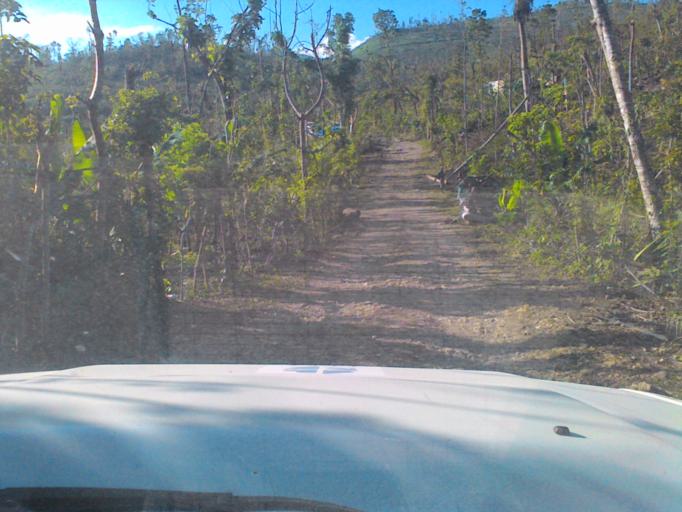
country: HT
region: Grandans
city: Jeremie
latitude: 18.5186
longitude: -74.0824
